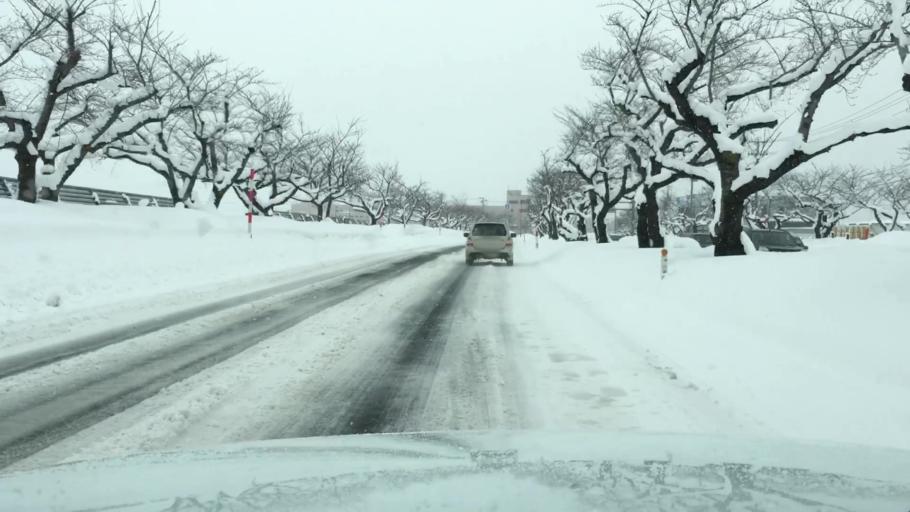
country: JP
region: Aomori
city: Hirosaki
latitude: 40.6382
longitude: 140.4890
